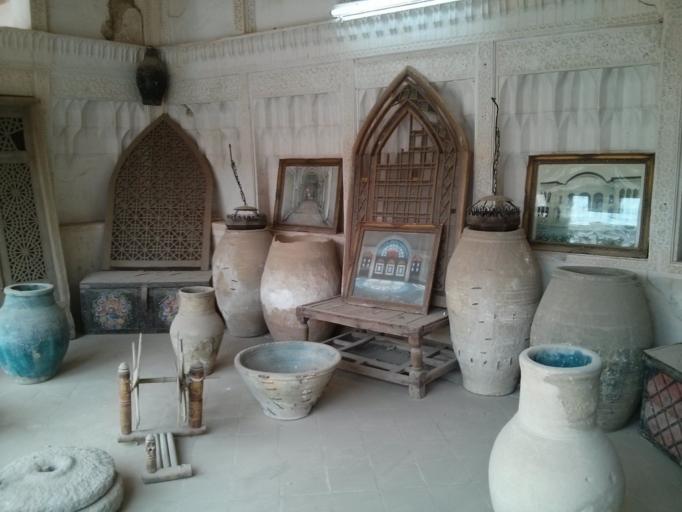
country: IR
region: Isfahan
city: Kashan
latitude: 33.9764
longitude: 51.4405
